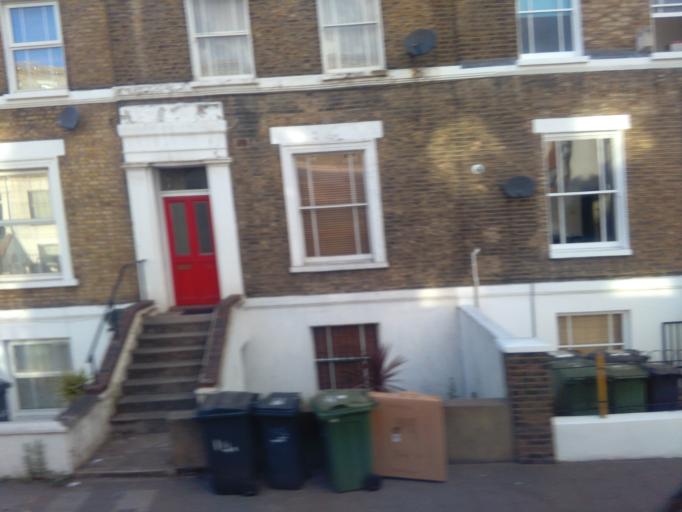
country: GB
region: England
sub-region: Greater London
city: Brixton
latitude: 51.4678
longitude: -0.0990
